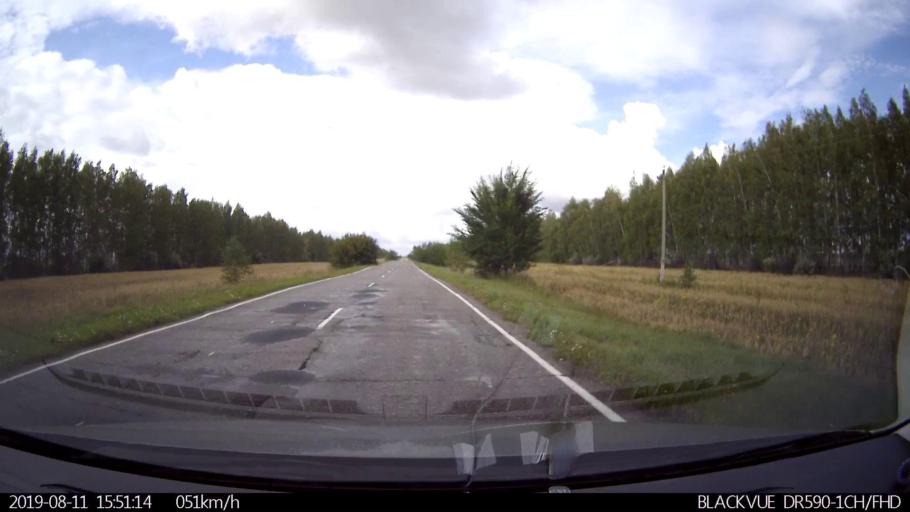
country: RU
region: Ulyanovsk
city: Ignatovka
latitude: 53.9173
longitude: 47.6560
